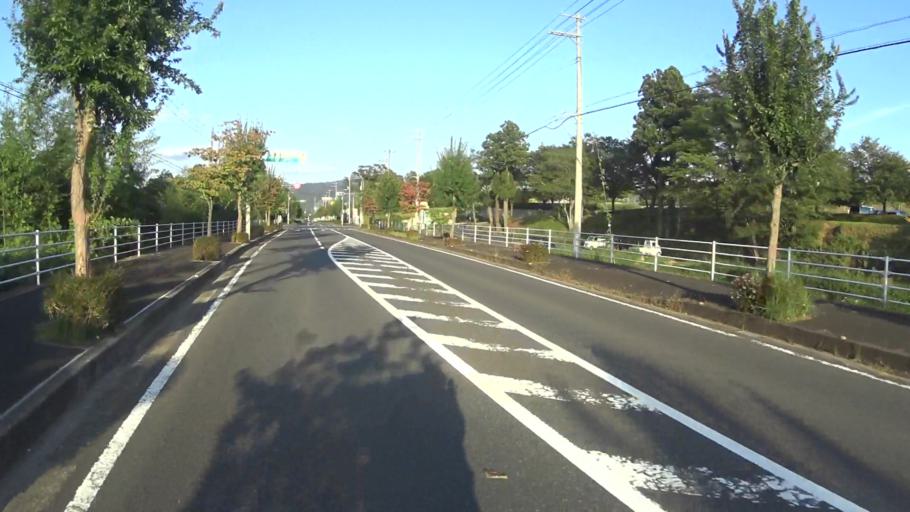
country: JP
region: Kyoto
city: Miyazu
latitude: 35.6068
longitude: 135.0571
